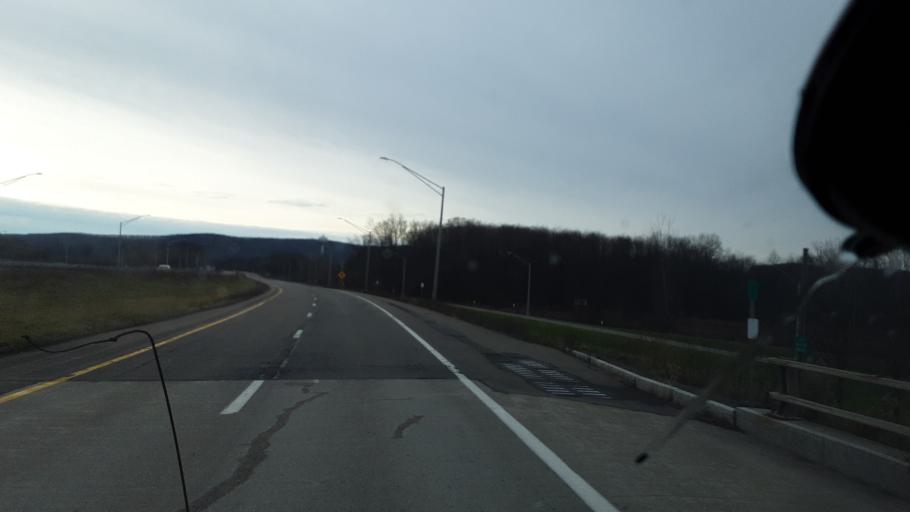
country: US
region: New York
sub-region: Cattaraugus County
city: Salamanca
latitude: 42.1547
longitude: -78.7506
